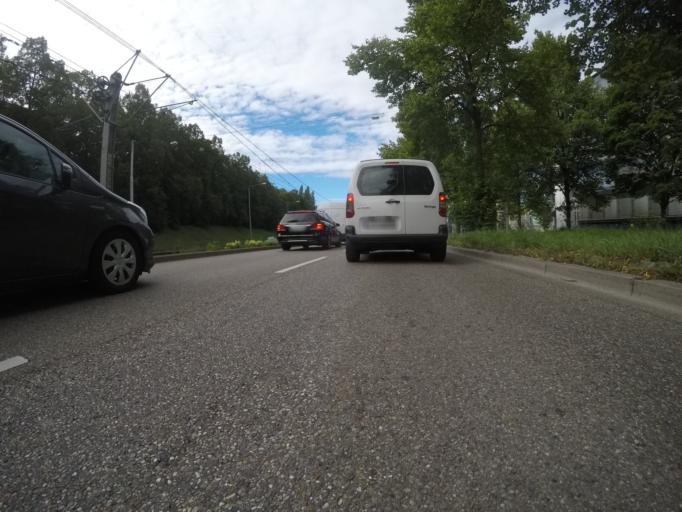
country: DE
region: Baden-Wuerttemberg
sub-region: Regierungsbezirk Stuttgart
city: Stuttgart
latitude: 48.8025
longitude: 9.1834
